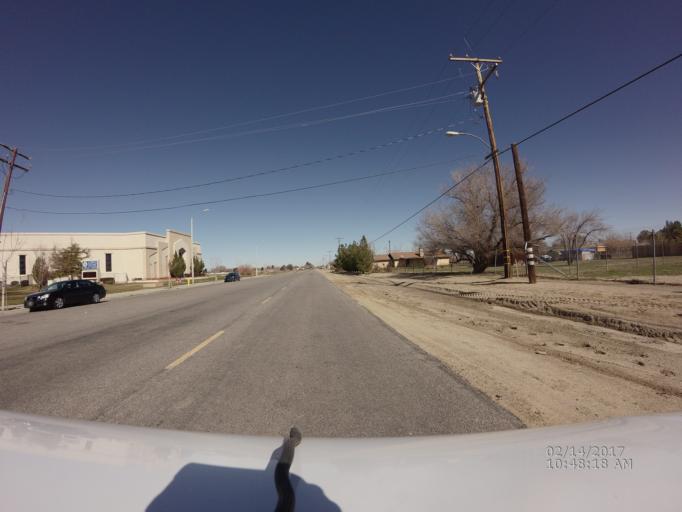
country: US
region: California
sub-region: Los Angeles County
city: Littlerock
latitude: 34.5679
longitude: -117.9521
